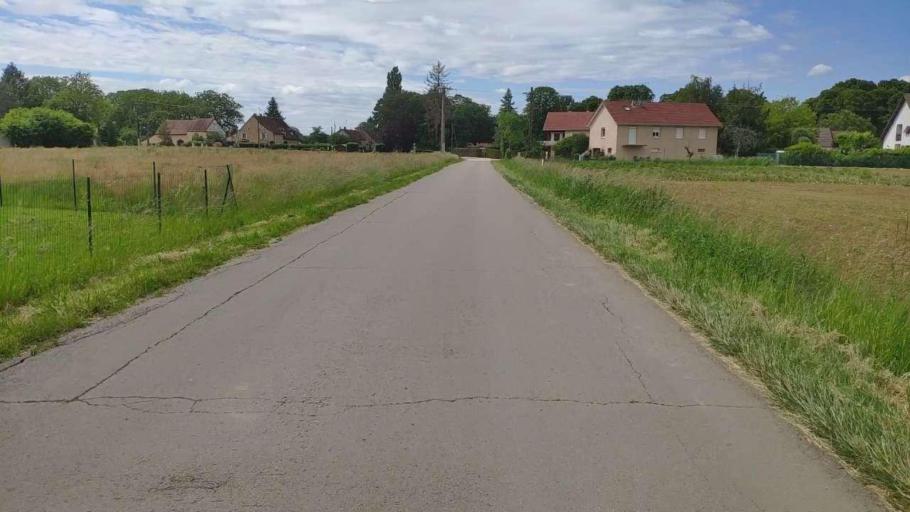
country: FR
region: Franche-Comte
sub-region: Departement du Jura
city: Bletterans
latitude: 46.7397
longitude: 5.5016
